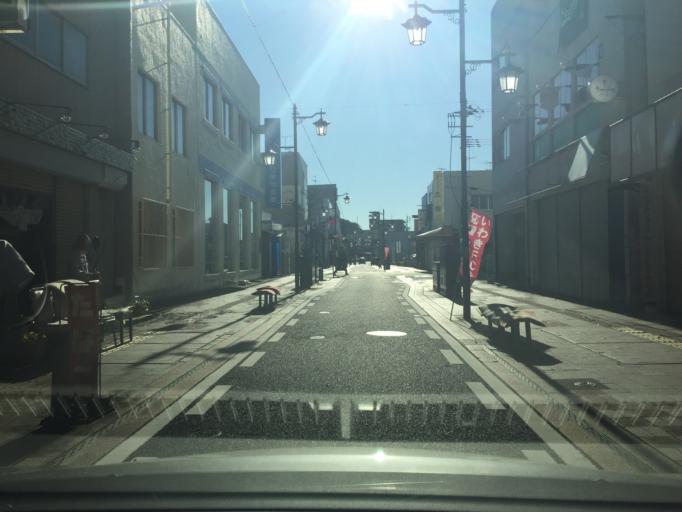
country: JP
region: Fukushima
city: Iwaki
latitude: 37.0088
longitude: 140.8475
